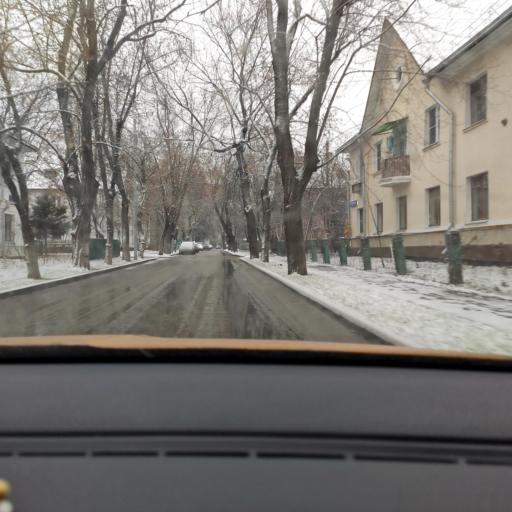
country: RU
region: Moskovskaya
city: Kur'yanovo
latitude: 55.6562
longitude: 37.7014
